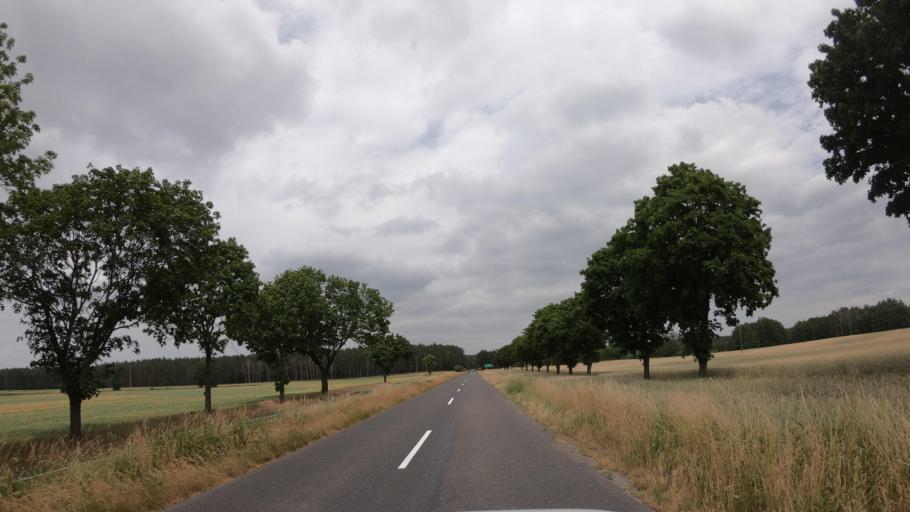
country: PL
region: West Pomeranian Voivodeship
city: Trzcinsko Zdroj
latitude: 52.9863
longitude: 14.7193
